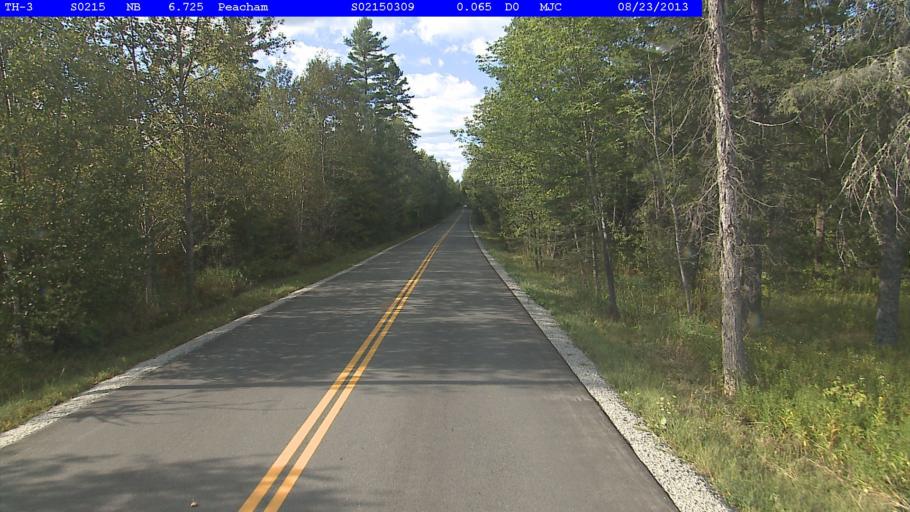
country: US
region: Vermont
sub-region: Caledonia County
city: Saint Johnsbury
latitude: 44.2988
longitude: -72.1633
